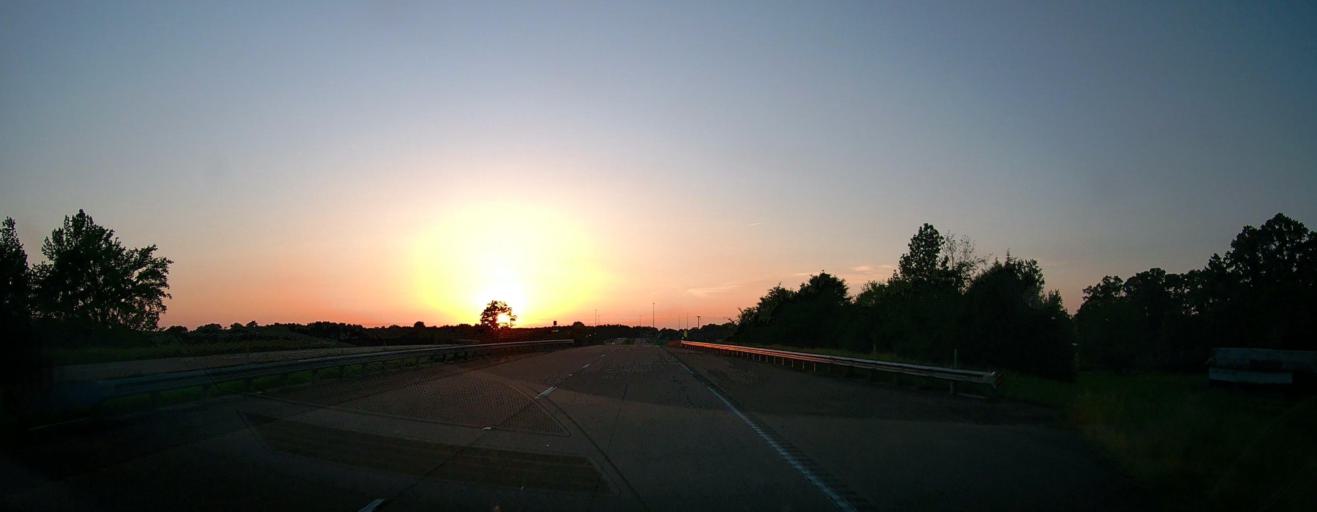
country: US
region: Mississippi
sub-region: Union County
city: New Albany
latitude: 34.4657
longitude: -88.9978
